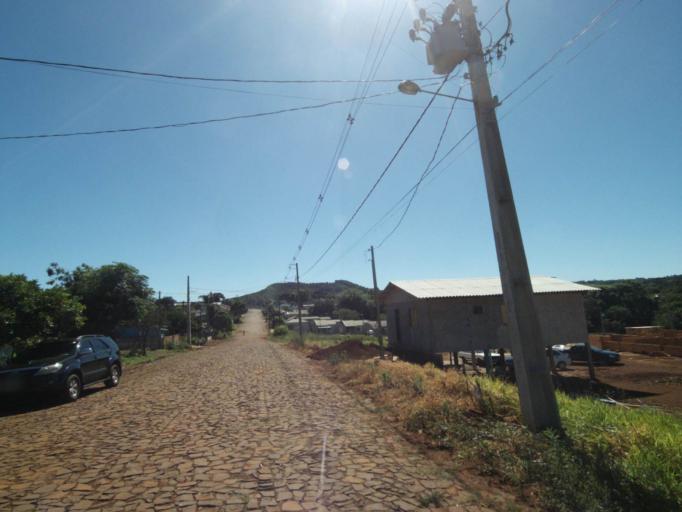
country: BR
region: Santa Catarina
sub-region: Sao Lourenco Do Oeste
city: Sao Lourenco dOeste
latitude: -26.2713
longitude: -52.7836
